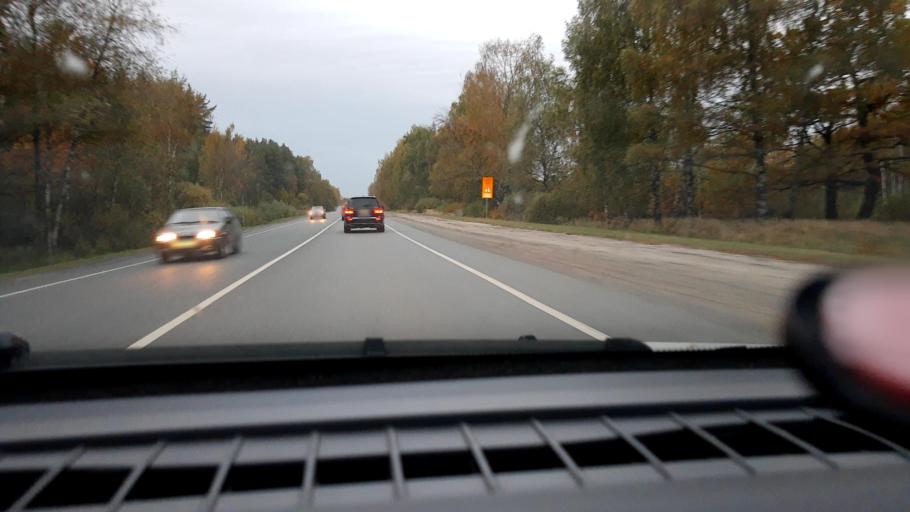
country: RU
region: Vladimir
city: Orgtrud
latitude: 56.2100
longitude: 40.6112
